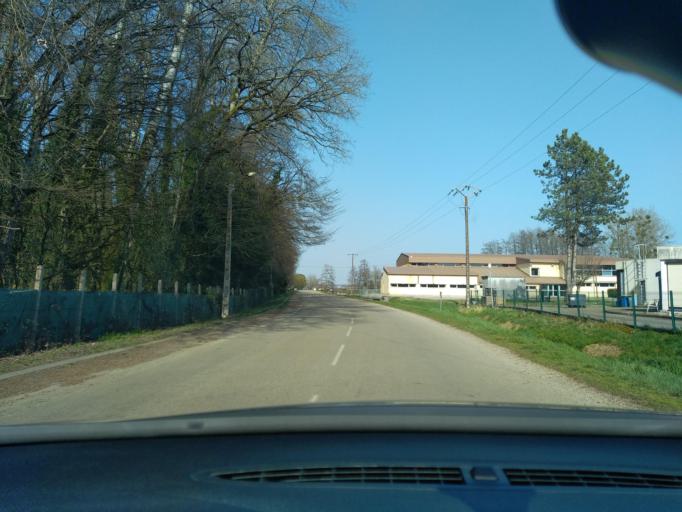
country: FR
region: Franche-Comte
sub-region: Departement du Jura
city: Mont-sous-Vaudrey
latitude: 46.9824
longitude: 5.6046
